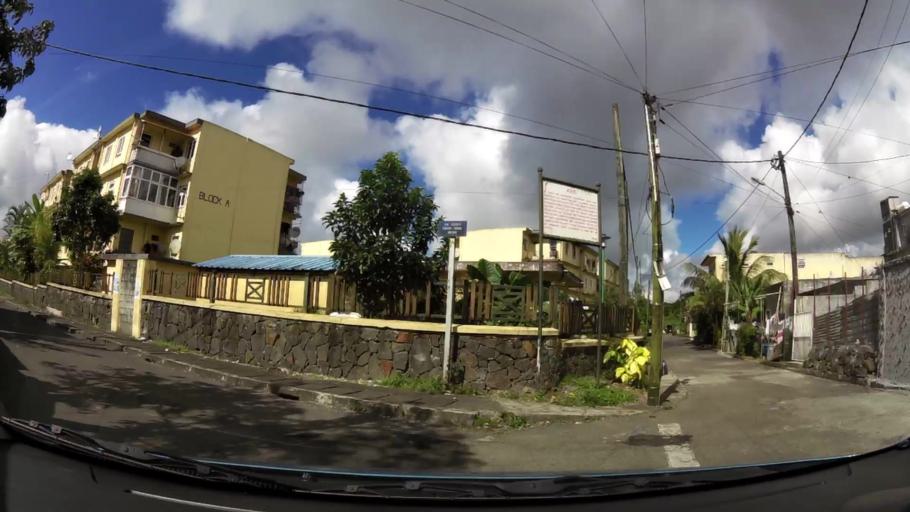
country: MU
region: Plaines Wilhems
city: Curepipe
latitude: -20.3340
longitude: 57.5260
